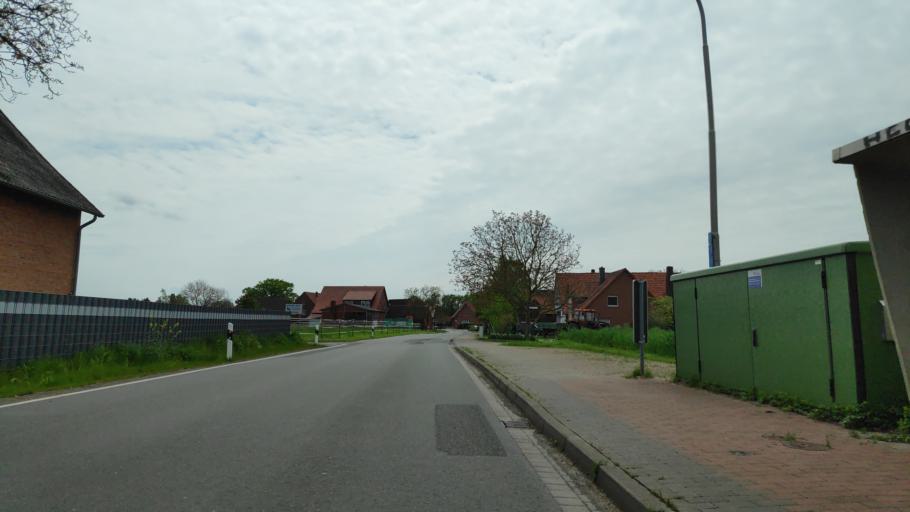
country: DE
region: North Rhine-Westphalia
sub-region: Regierungsbezirk Detmold
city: Petershagen
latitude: 52.3193
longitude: 8.9952
